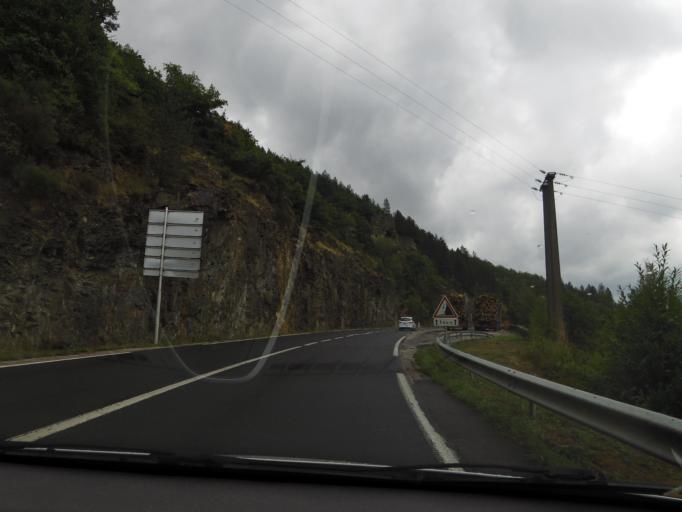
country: FR
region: Languedoc-Roussillon
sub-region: Departement de la Lozere
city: Florac
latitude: 44.3622
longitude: 3.5674
